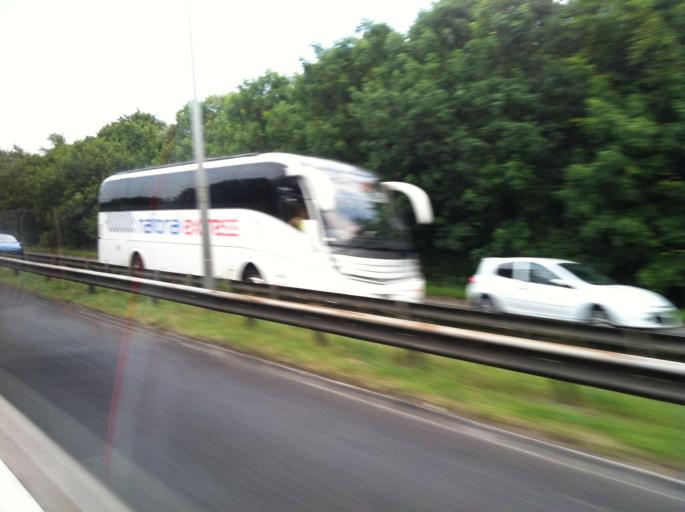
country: GB
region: Wales
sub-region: Vale of Glamorgan
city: Dinas Powys
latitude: 51.4741
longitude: -3.2282
